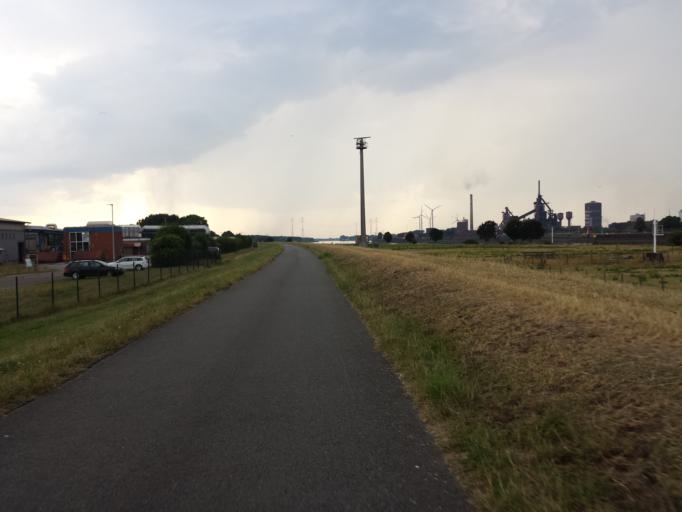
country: DE
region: Lower Saxony
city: Ritterhude
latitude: 53.1160
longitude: 8.7129
